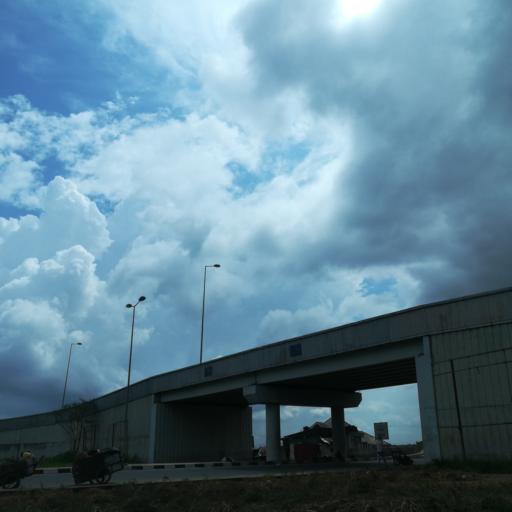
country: NG
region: Rivers
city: Port Harcourt
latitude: 4.8095
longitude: 7.0627
